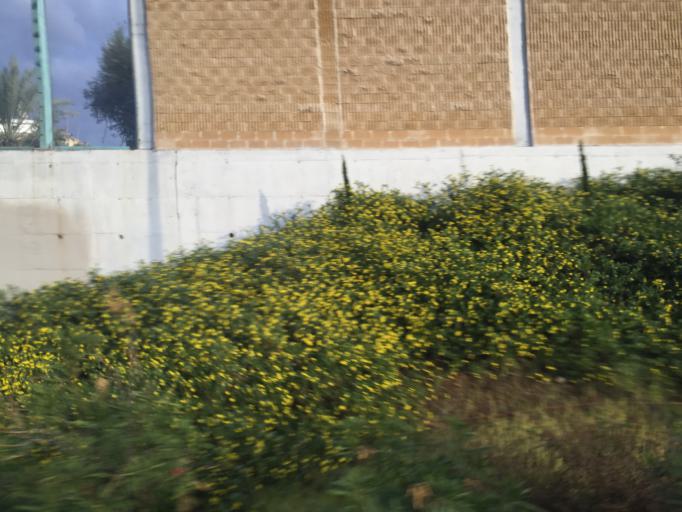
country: IL
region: Tel Aviv
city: Tel Aviv
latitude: 32.0558
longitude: 34.7857
